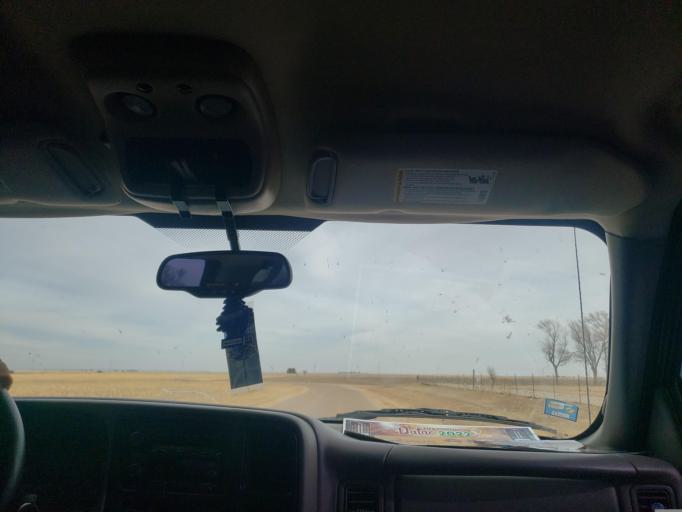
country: US
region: Kansas
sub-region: Finney County
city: Garden City
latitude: 37.9236
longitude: -100.7155
